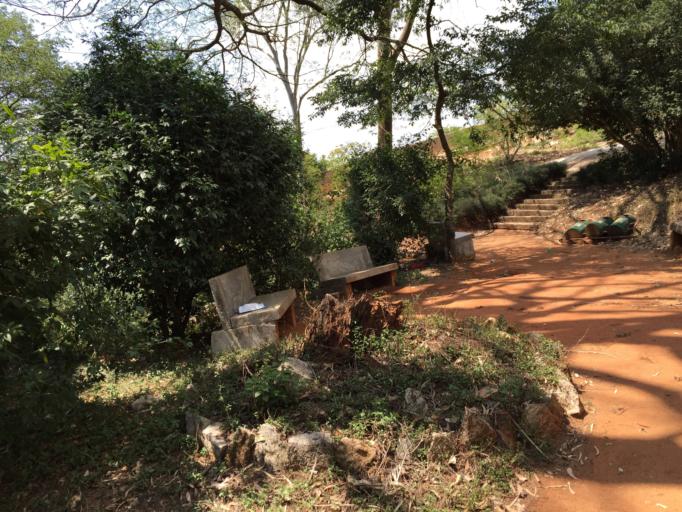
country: IN
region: Karnataka
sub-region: Chikkaballapur
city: Chik Ballapur
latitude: 13.3716
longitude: 77.6833
